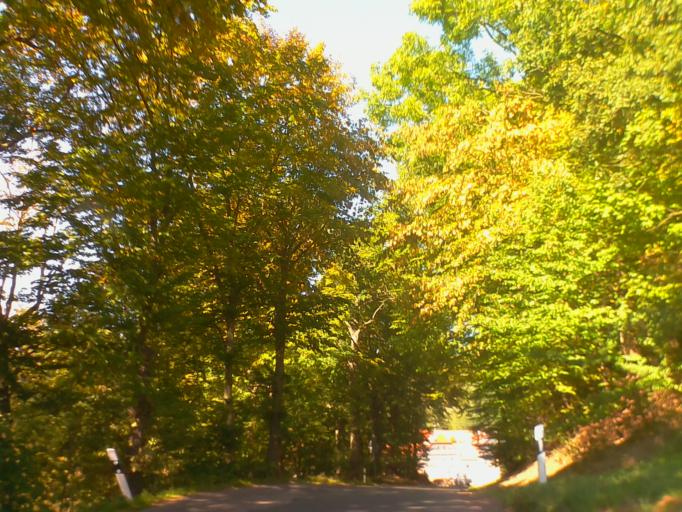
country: DE
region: Thuringia
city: Ottendorf
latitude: 50.8245
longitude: 11.8236
